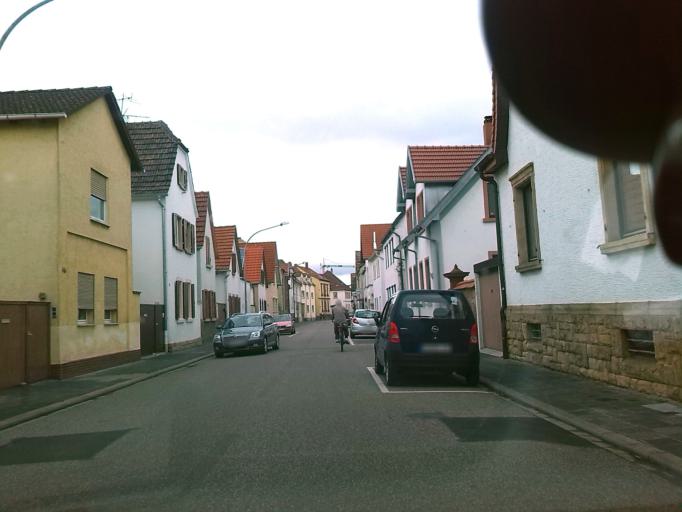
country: DE
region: Rheinland-Pfalz
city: Hassloch
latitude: 49.3684
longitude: 8.2546
